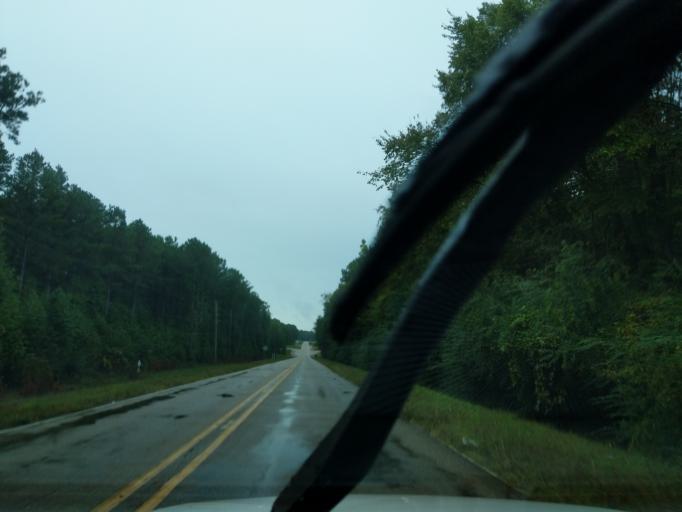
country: US
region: Louisiana
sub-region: Bienville Parish
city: Arcadia
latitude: 32.5570
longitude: -93.0541
